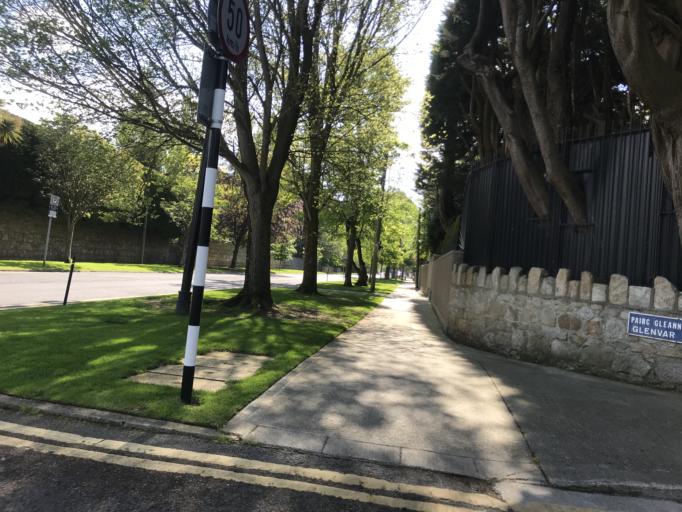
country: IE
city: Booterstown
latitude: 53.3019
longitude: -6.1932
